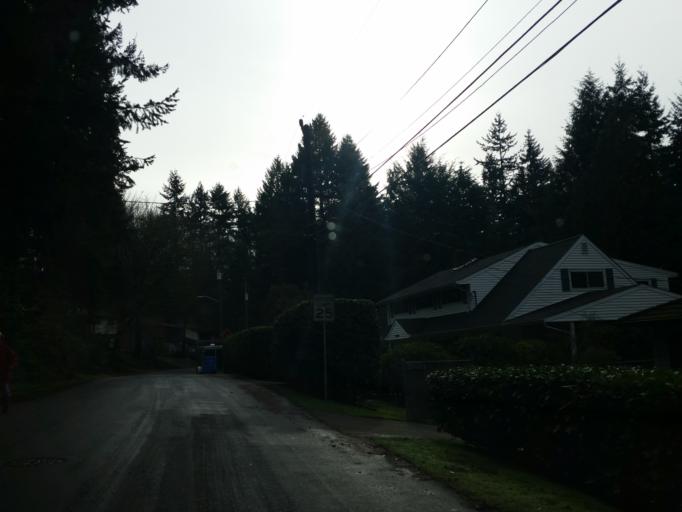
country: US
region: Washington
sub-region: King County
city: Shoreline
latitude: 47.7555
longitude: -122.3535
